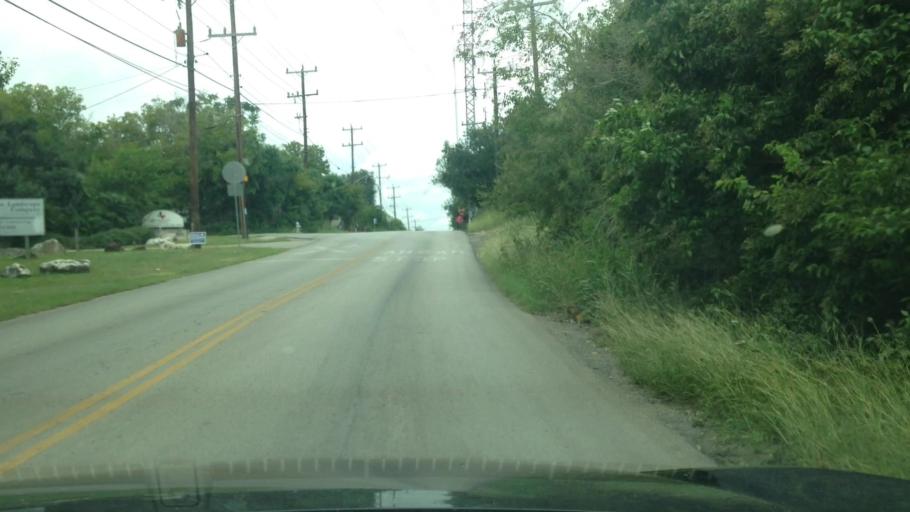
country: US
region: Texas
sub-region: Bexar County
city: Windcrest
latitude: 29.5758
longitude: -98.4073
